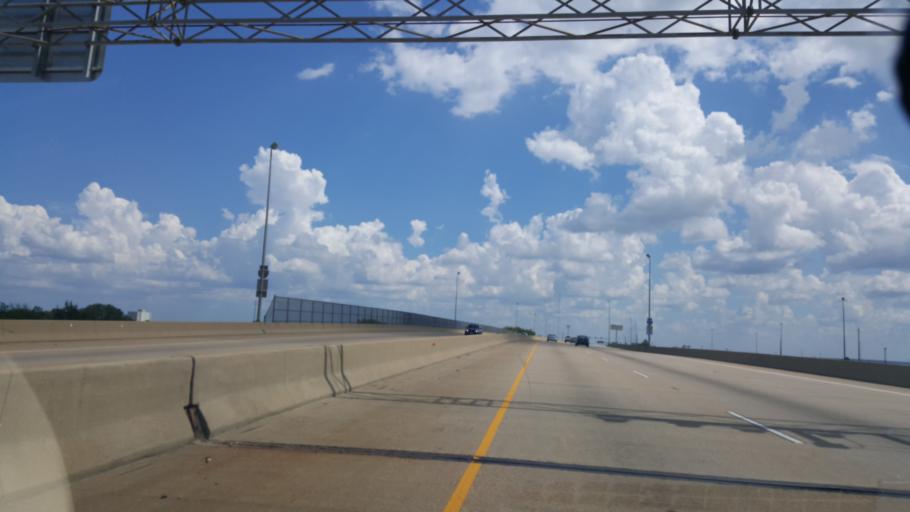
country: US
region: Virginia
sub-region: City of Newport News
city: Newport News
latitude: 36.9753
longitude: -76.4212
